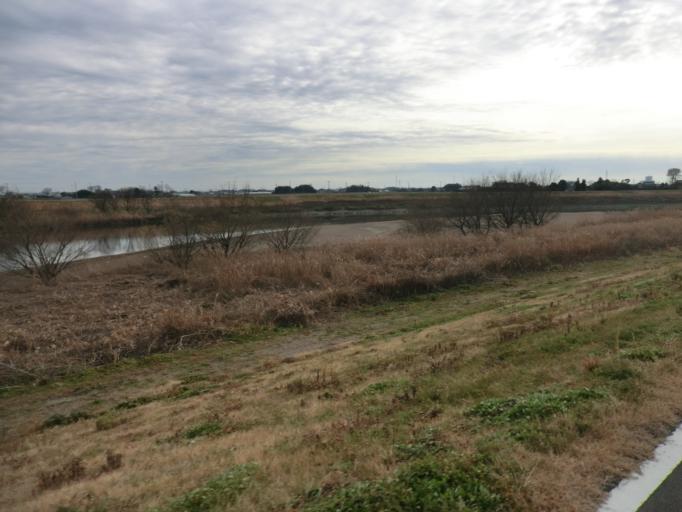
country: JP
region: Ibaraki
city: Mitsukaido
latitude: 35.9973
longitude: 139.9909
